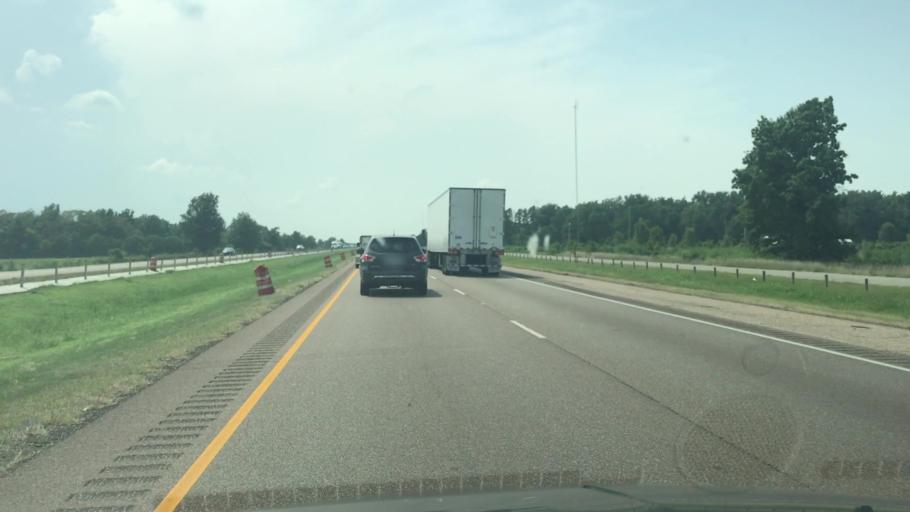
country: US
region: Arkansas
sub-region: Crittenden County
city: Earle
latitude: 35.1505
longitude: -90.3753
